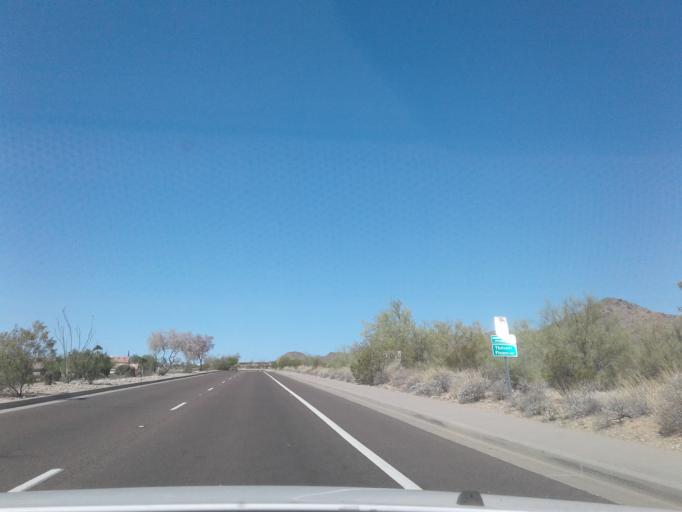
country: US
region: Arizona
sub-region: Maricopa County
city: Fountain Hills
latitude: 33.6091
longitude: -111.7441
